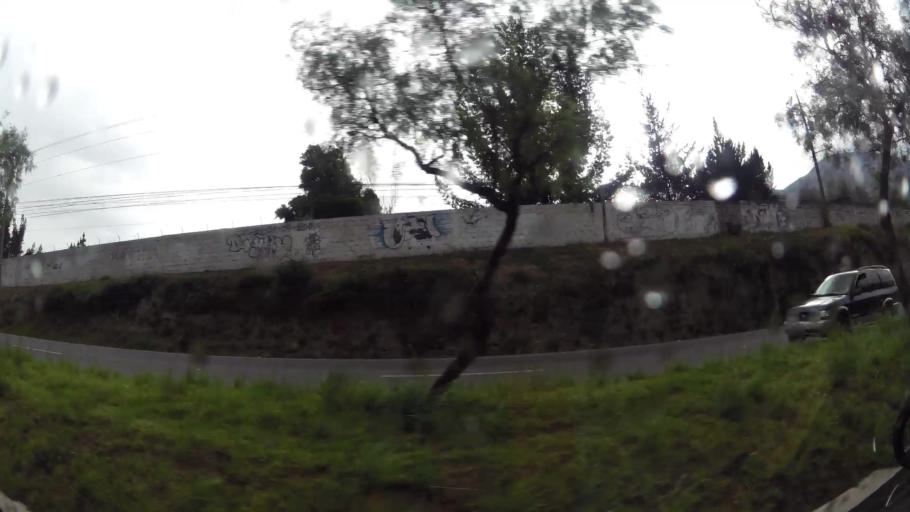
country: EC
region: Pichincha
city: Quito
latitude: -0.0826
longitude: -78.4832
